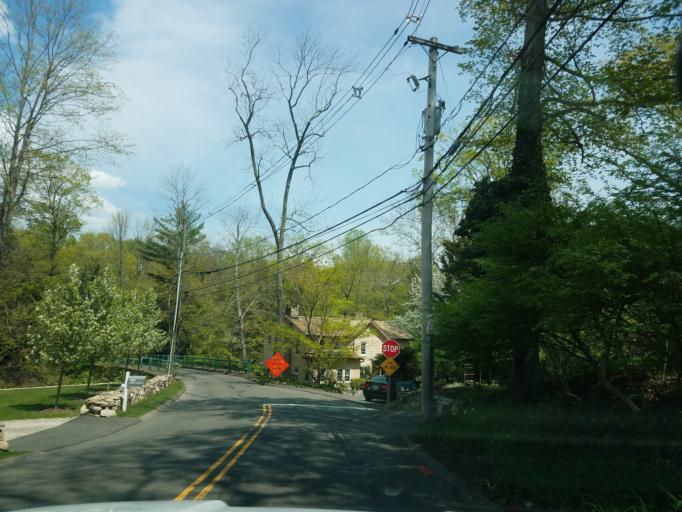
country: US
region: Connecticut
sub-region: Fairfield County
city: Wilton
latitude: 41.1510
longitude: -73.4460
